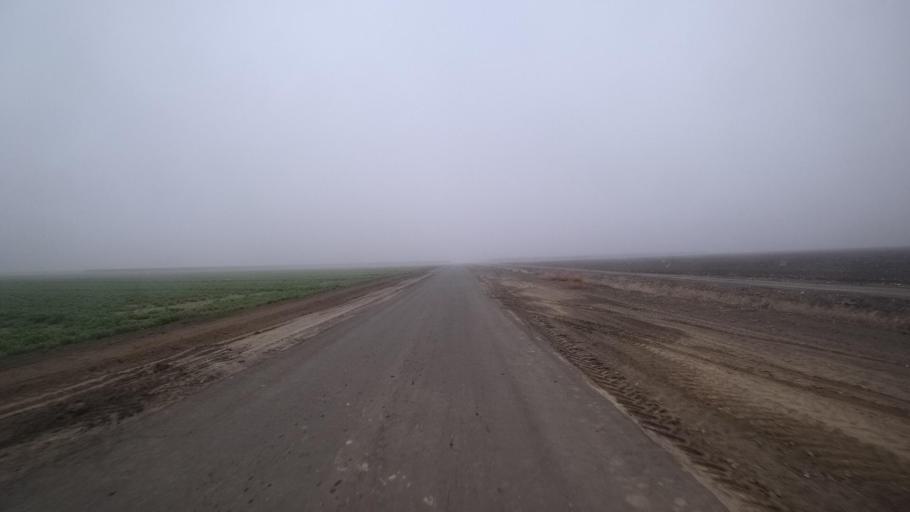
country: US
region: California
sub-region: Kern County
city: Buttonwillow
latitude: 35.4563
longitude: -119.5442
